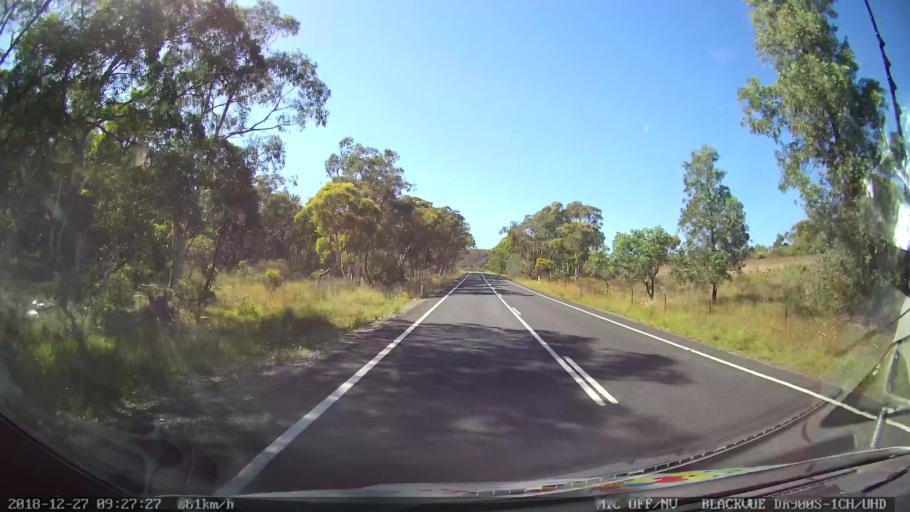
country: AU
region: New South Wales
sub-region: Lithgow
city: Portland
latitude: -33.1529
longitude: 149.9936
